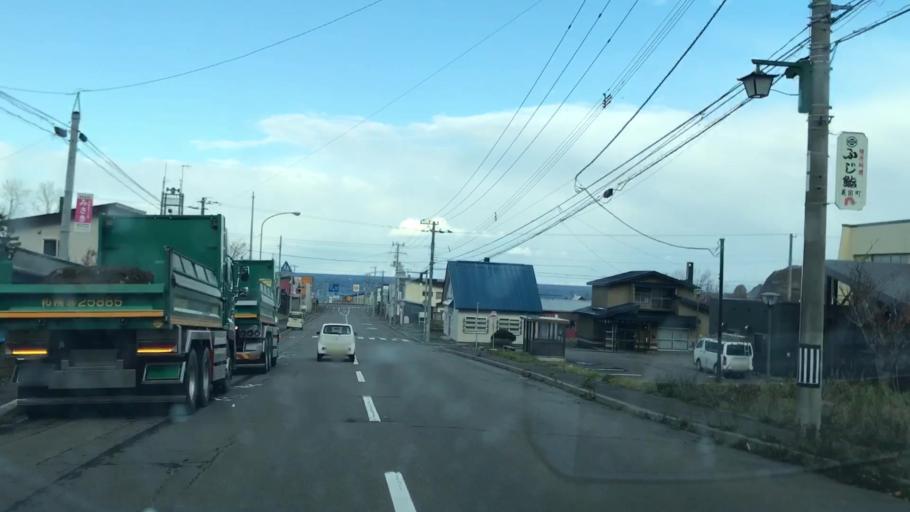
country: JP
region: Hokkaido
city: Yoichi
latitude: 43.3404
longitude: 140.4585
